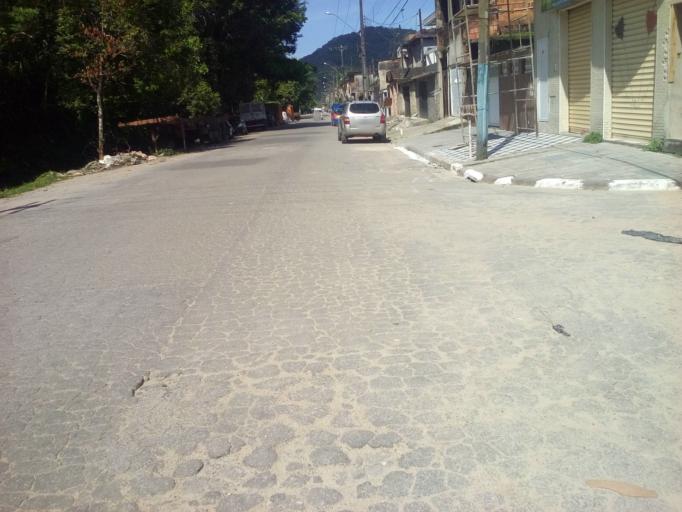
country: BR
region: Sao Paulo
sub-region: Guaruja
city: Guaruja
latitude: -23.9604
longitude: -46.2531
